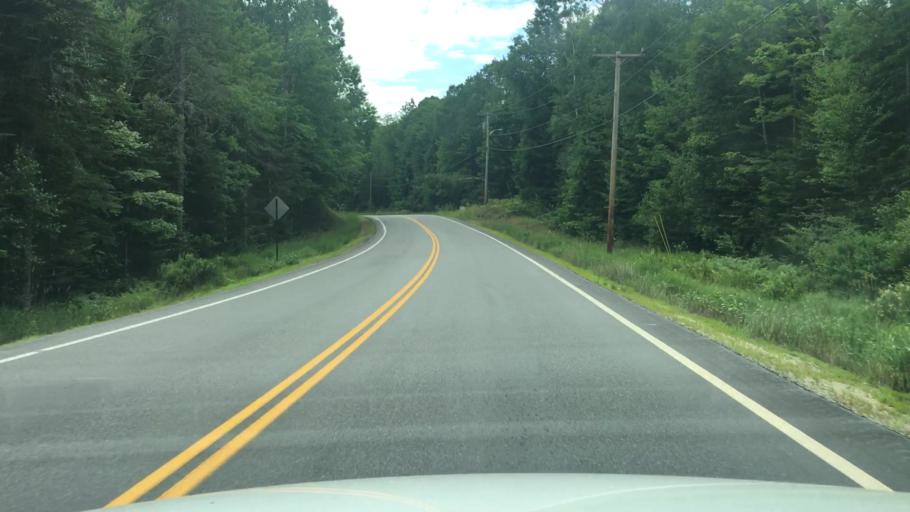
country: US
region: Maine
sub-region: Oxford County
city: West Paris
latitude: 44.3456
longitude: -70.5285
